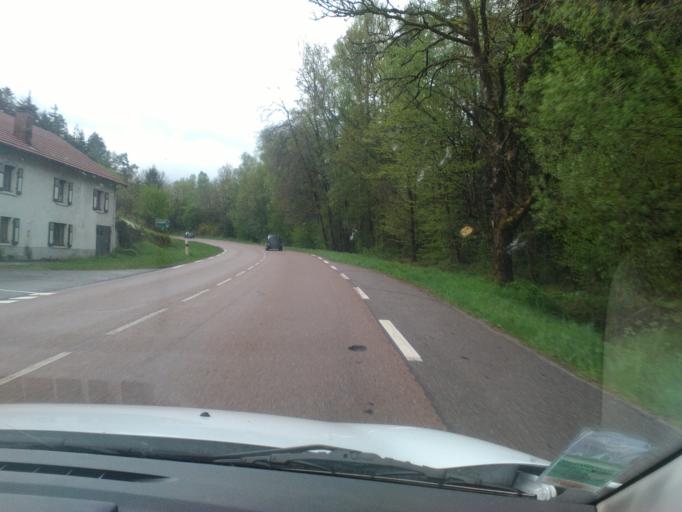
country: FR
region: Lorraine
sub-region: Departement des Vosges
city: Vagney
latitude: 47.9837
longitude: 6.7227
